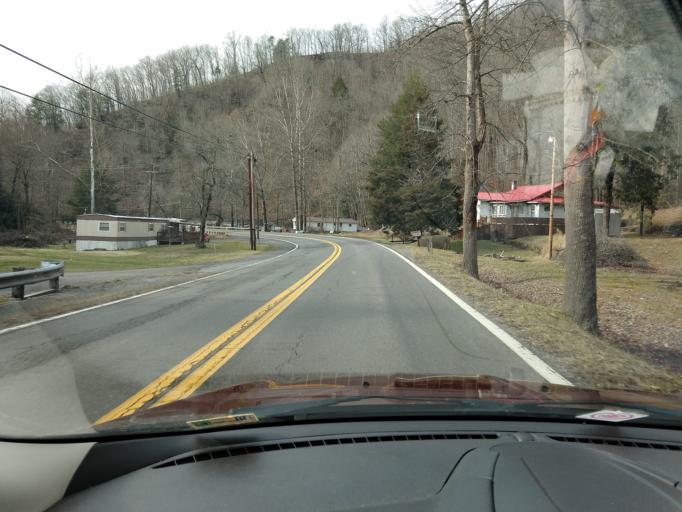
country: US
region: West Virginia
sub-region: McDowell County
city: Welch
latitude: 37.5052
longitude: -81.5590
